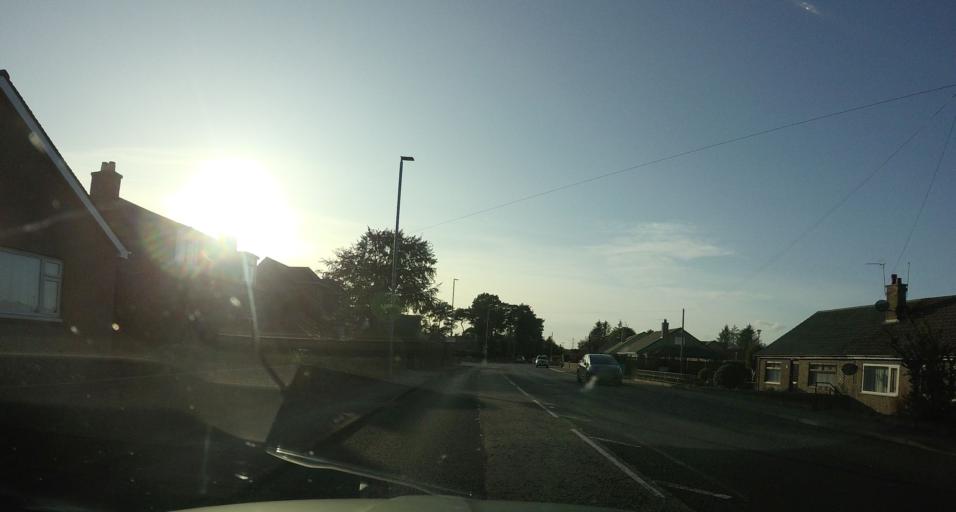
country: GB
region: Scotland
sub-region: Aberdeenshire
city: Westhill
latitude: 57.1498
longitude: -2.2980
